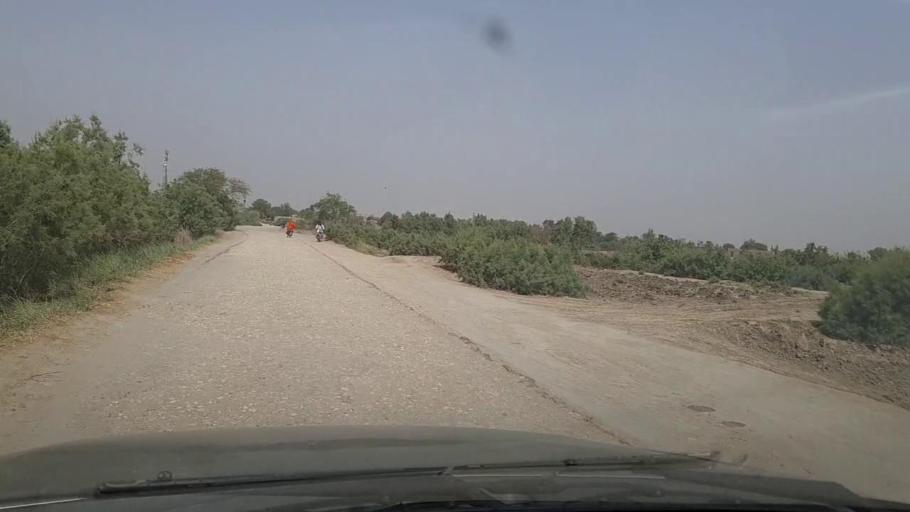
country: PK
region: Balochistan
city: Sohbatpur
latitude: 28.4233
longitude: 68.6767
